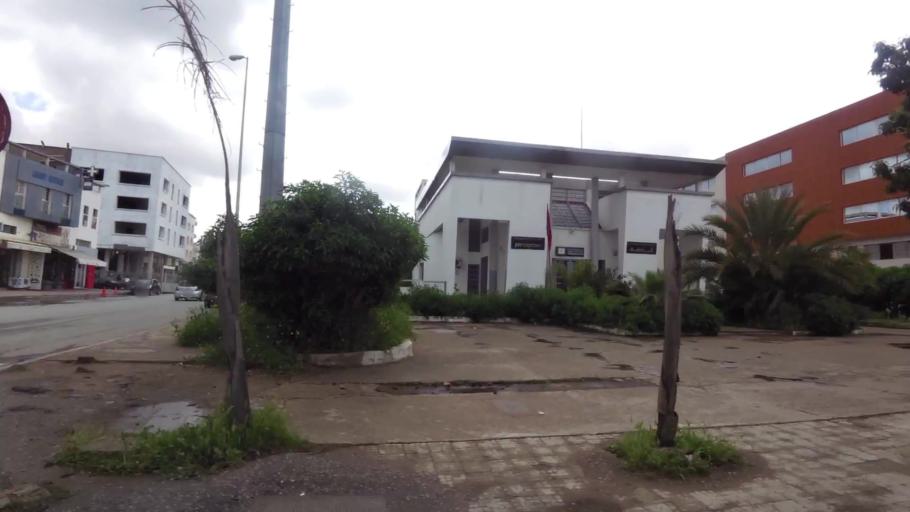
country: MA
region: Grand Casablanca
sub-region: Nouaceur
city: Bouskoura
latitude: 33.5220
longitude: -7.6519
